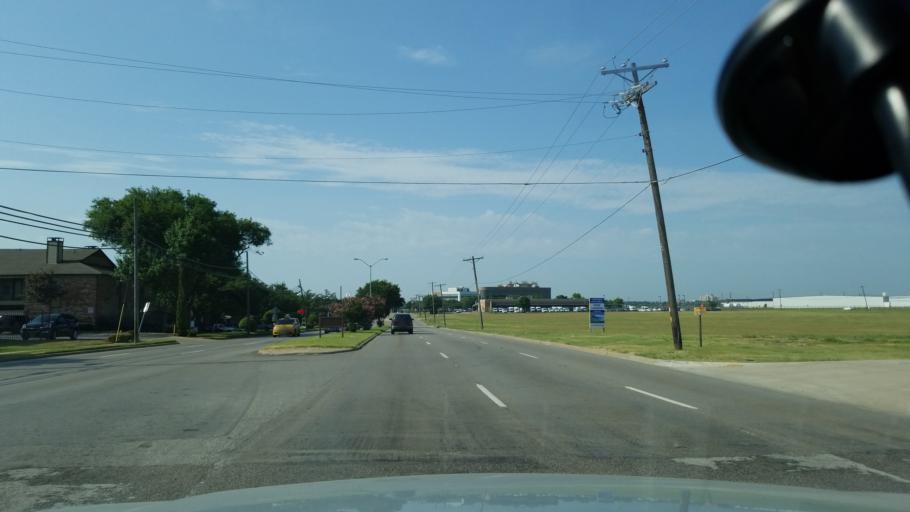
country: US
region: Texas
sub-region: Dallas County
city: Duncanville
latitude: 32.6829
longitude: -96.8571
